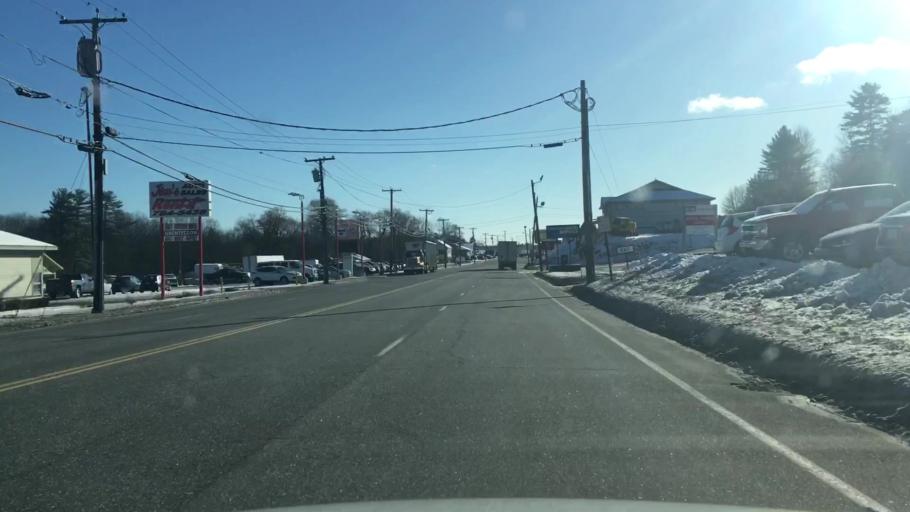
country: US
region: Maine
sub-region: Androscoggin County
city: Lewiston
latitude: 44.1397
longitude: -70.2263
